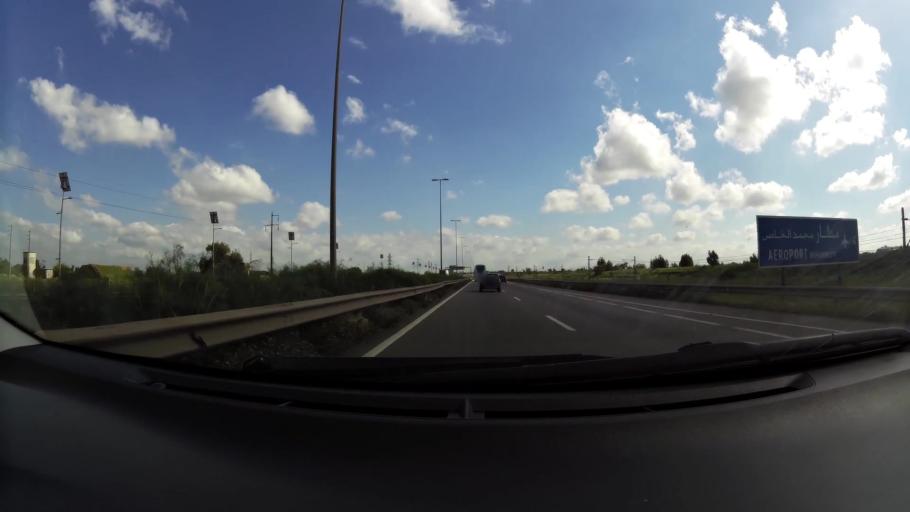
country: MA
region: Grand Casablanca
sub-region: Nouaceur
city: Bouskoura
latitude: 33.4300
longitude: -7.6278
